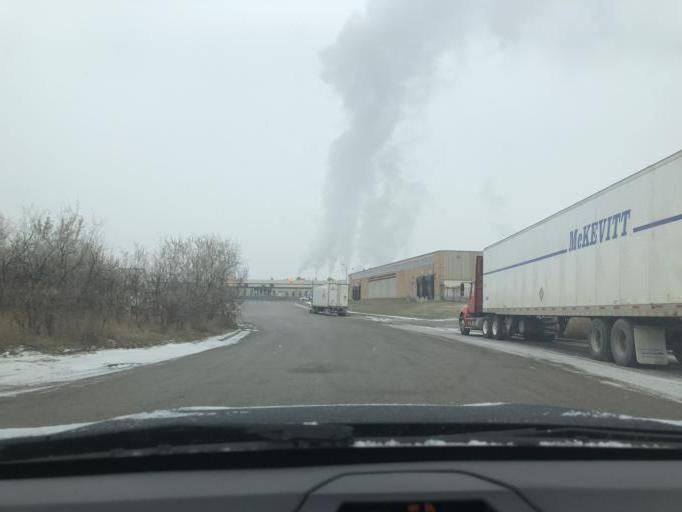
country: CA
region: Ontario
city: Scarborough
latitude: 43.7761
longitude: -79.2664
